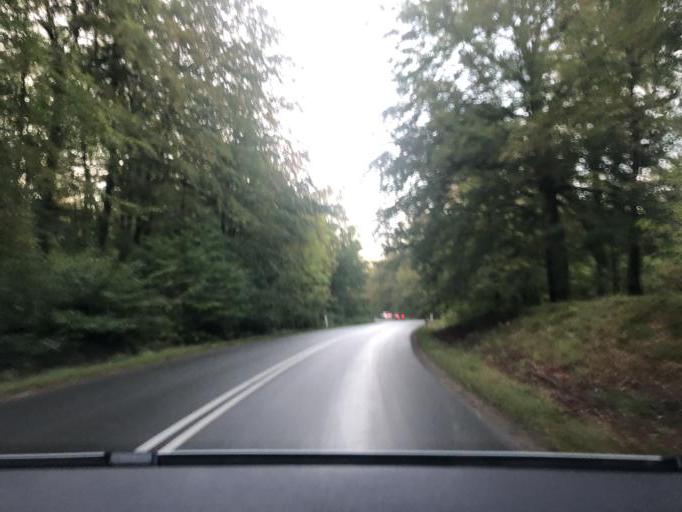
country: DK
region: Capital Region
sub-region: Frederikssund Kommune
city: Slangerup
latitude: 55.8157
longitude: 12.2040
